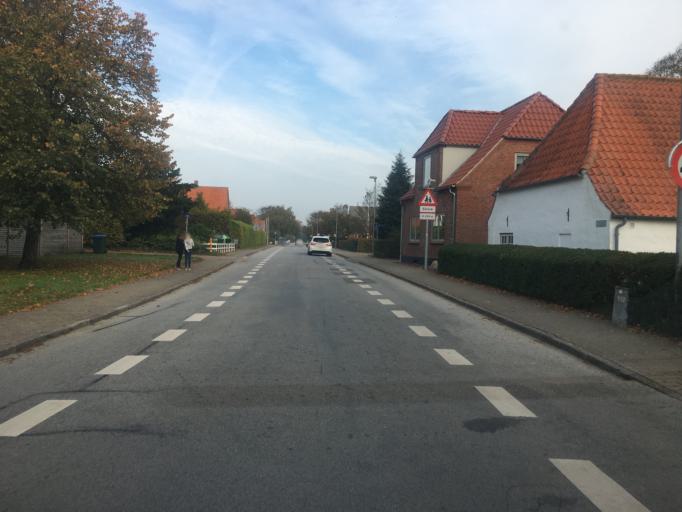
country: DK
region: South Denmark
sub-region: Tonder Kommune
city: Logumkloster
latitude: 55.0588
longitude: 8.9554
